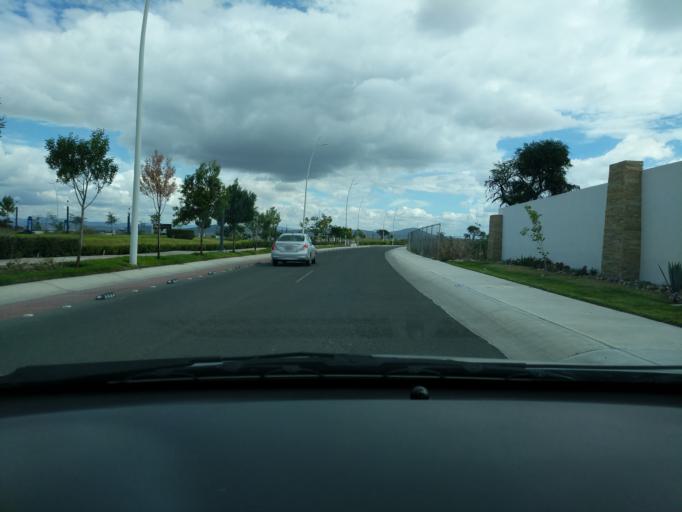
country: MX
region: Queretaro
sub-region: El Marques
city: La Pradera
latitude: 20.6601
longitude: -100.3131
